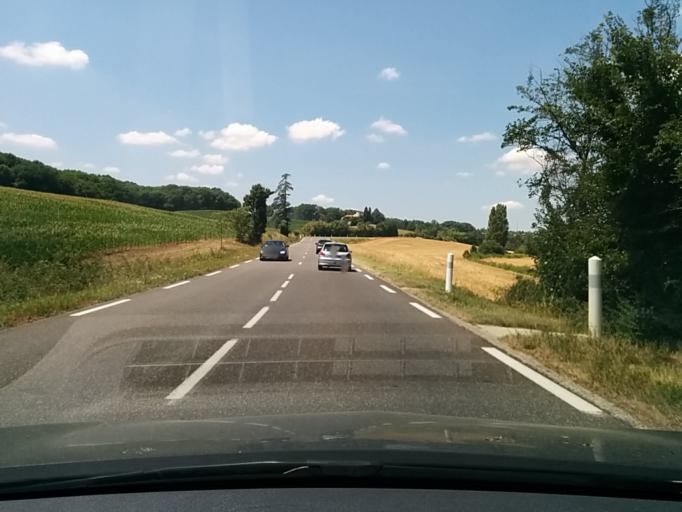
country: FR
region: Midi-Pyrenees
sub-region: Departement du Gers
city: Vic-Fezensac
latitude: 43.7424
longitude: 0.3542
